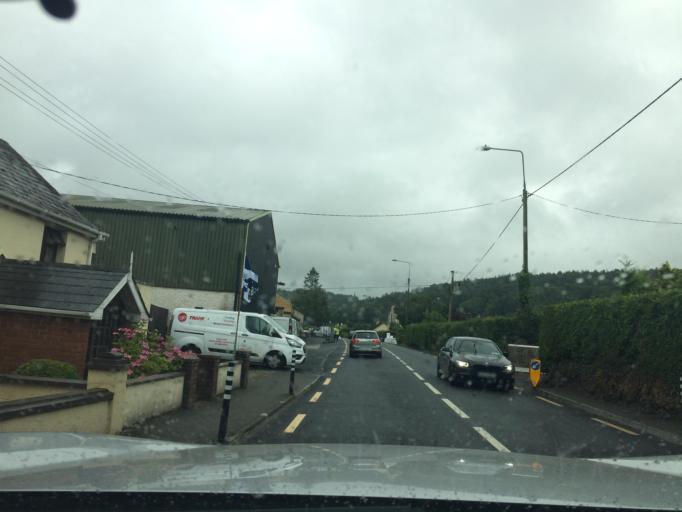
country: IE
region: Munster
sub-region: South Tipperary
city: Cluain Meala
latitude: 52.2680
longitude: -7.7216
